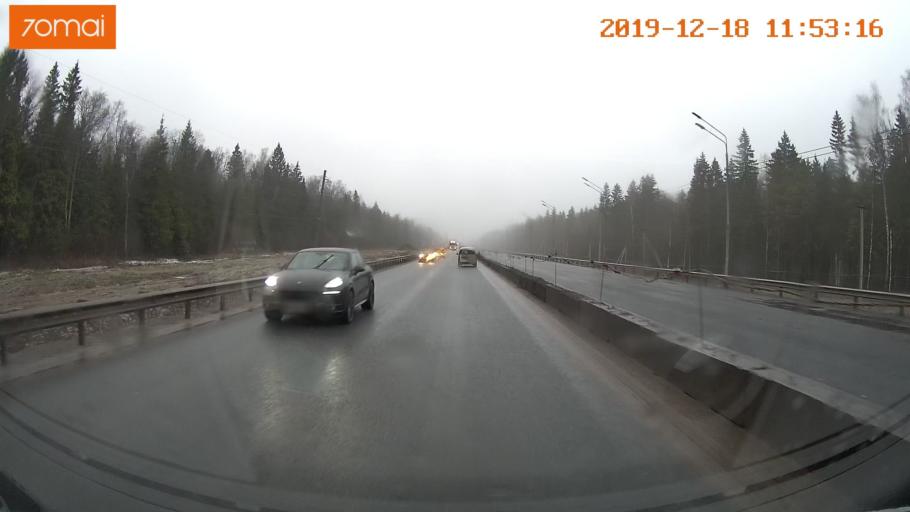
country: RU
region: Moskovskaya
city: Yershovo
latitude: 55.8024
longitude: 36.9199
